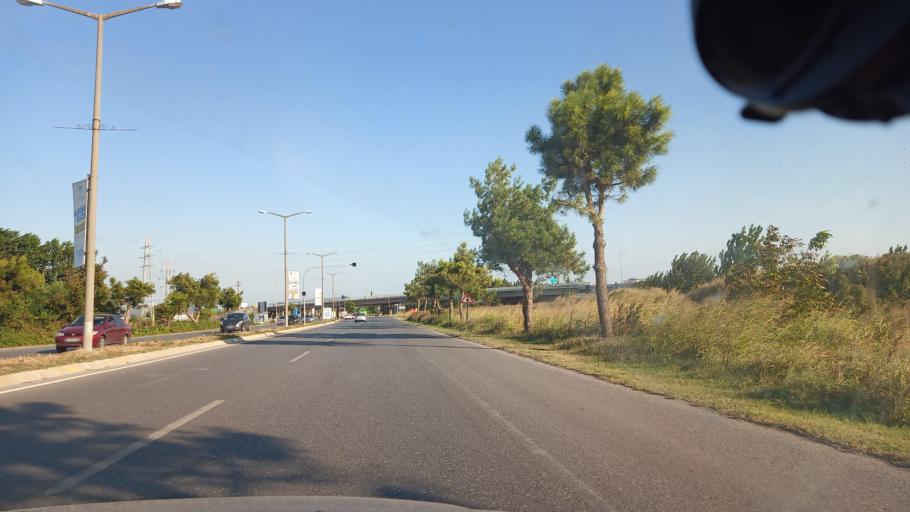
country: TR
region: Sakarya
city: Kazimpasa
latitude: 40.8461
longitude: 30.3274
